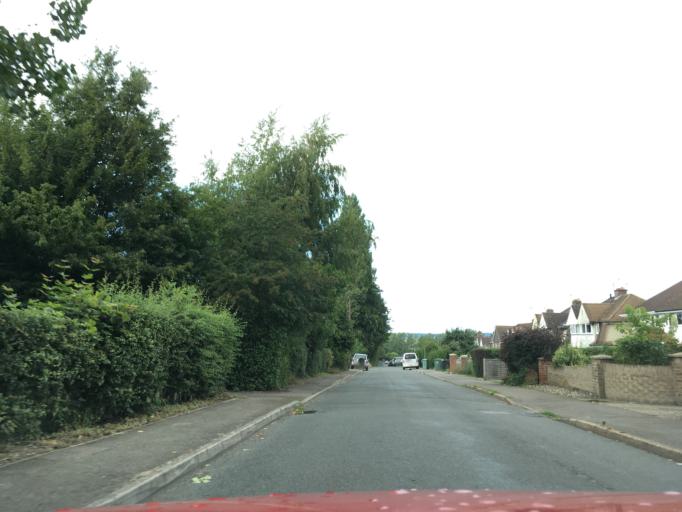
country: GB
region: England
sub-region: Kent
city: Maidstone
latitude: 51.2315
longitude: 0.5207
